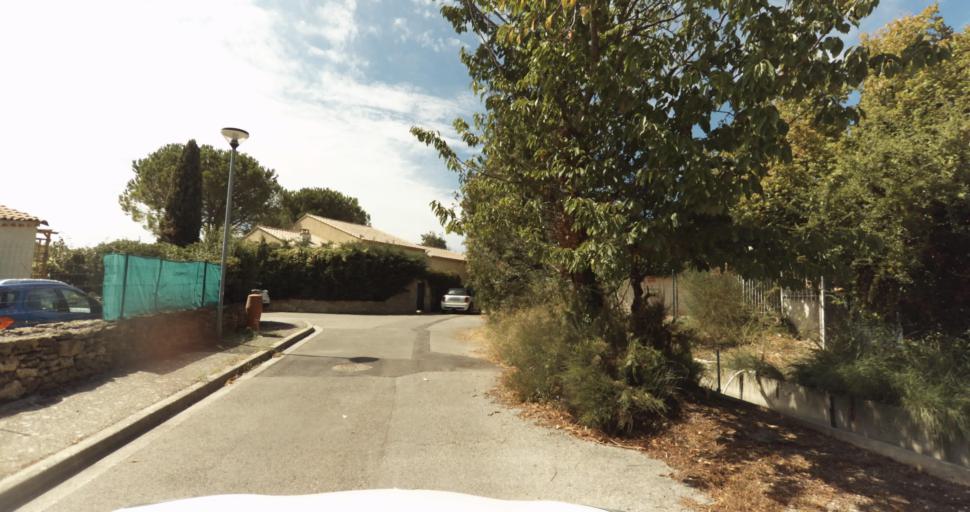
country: FR
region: Provence-Alpes-Cote d'Azur
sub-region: Departement des Bouches-du-Rhone
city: Miramas
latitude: 43.5806
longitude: 5.0205
